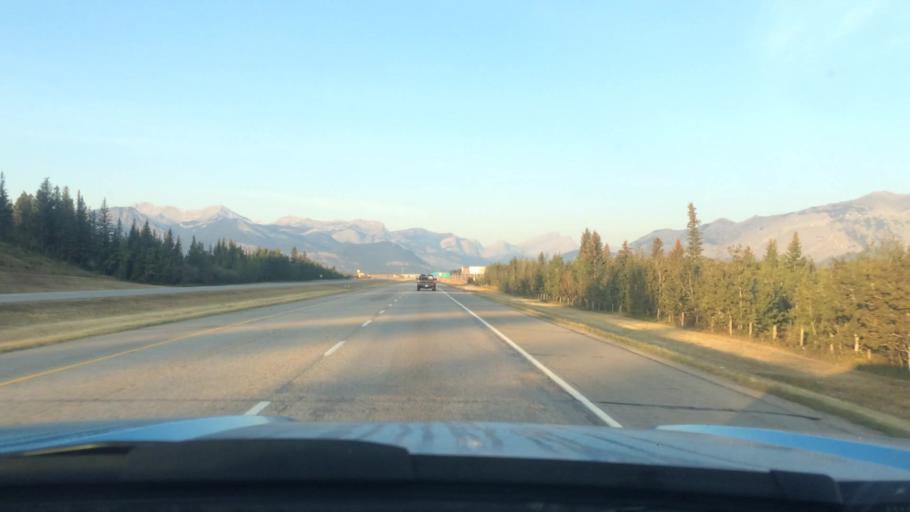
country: CA
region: Alberta
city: Canmore
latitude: 51.1139
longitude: -114.9963
